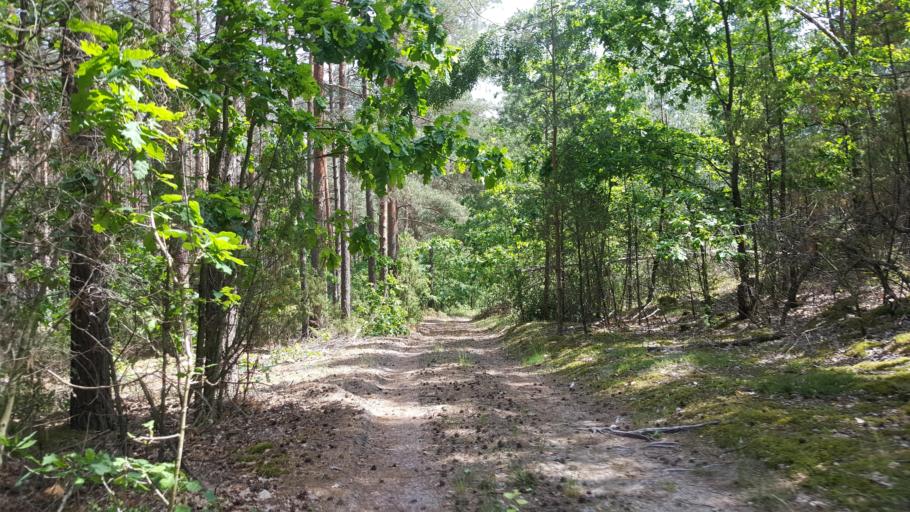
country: BY
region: Brest
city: Kamyanyuki
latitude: 52.5053
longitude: 23.8299
